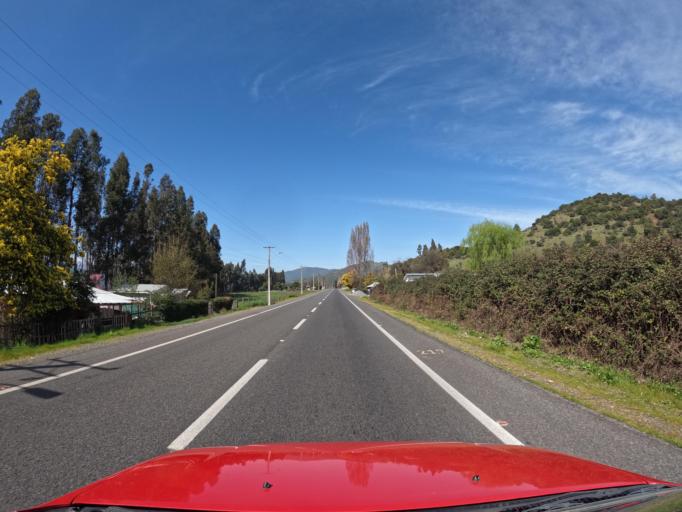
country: CL
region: Maule
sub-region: Provincia de Curico
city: Teno
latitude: -34.9788
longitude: -70.9628
